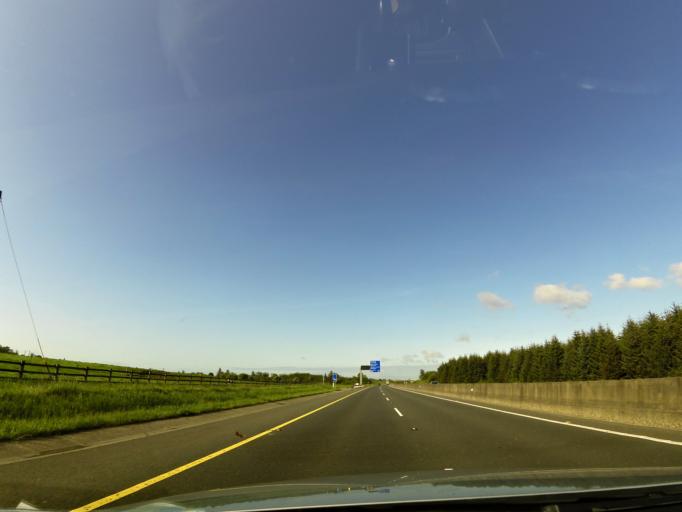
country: IE
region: Munster
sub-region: North Tipperary
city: Newport
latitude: 52.7613
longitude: -8.3987
